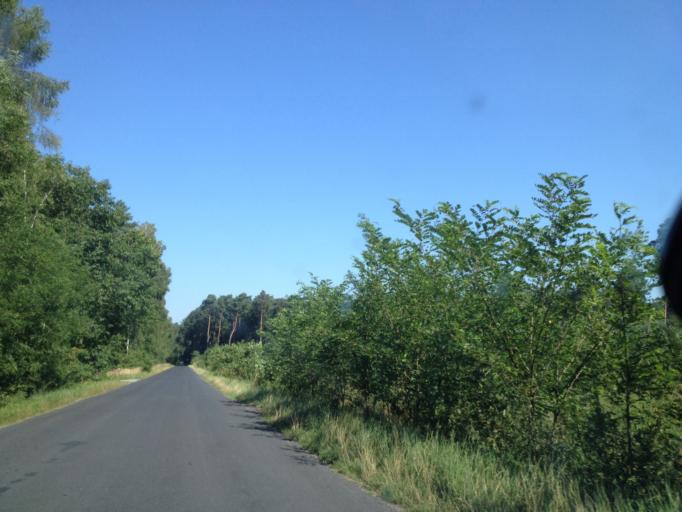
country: PL
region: Greater Poland Voivodeship
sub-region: Powiat sredzki
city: Zaniemysl
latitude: 52.1225
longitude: 17.1113
